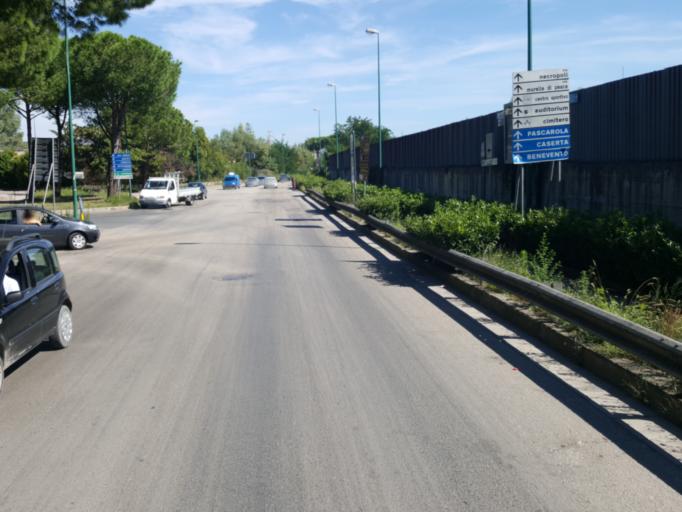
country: IT
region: Campania
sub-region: Provincia di Napoli
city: Caivano
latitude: 40.9657
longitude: 14.3034
